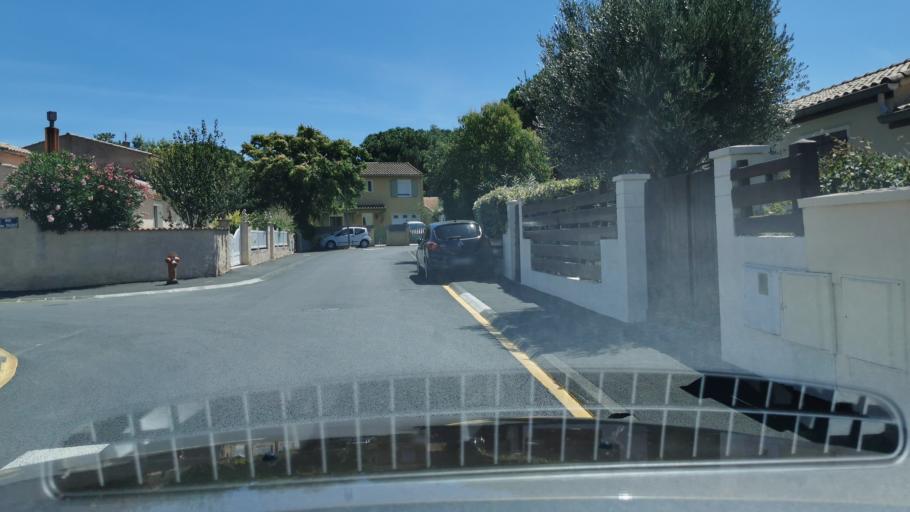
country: FR
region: Languedoc-Roussillon
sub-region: Departement de l'Aude
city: Armissan
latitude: 43.1872
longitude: 3.0971
